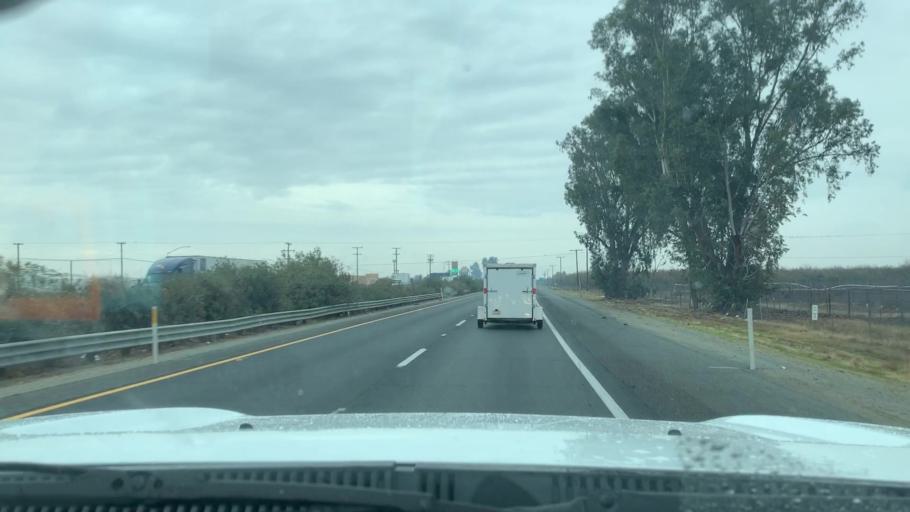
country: US
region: California
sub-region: Kern County
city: Delano
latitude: 35.8179
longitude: -119.2584
